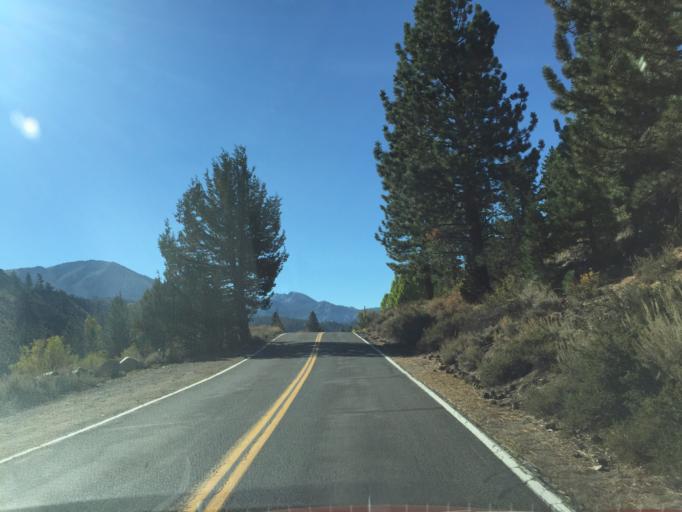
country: US
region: California
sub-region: Mono County
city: Bridgeport
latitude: 38.3292
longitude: -119.5522
